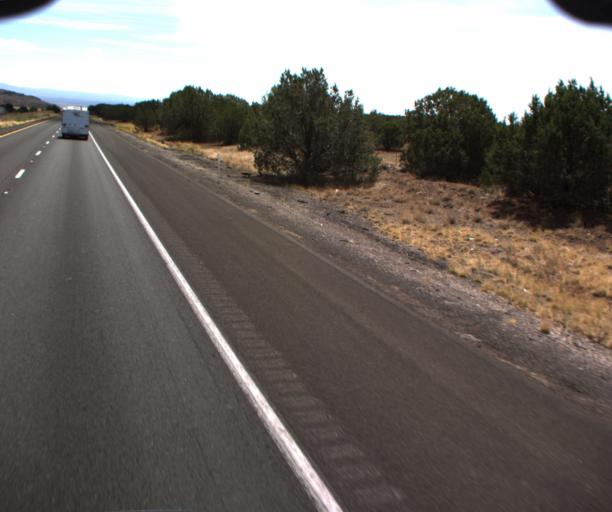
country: US
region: Arizona
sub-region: Yavapai County
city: Paulden
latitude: 35.2566
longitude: -112.7088
